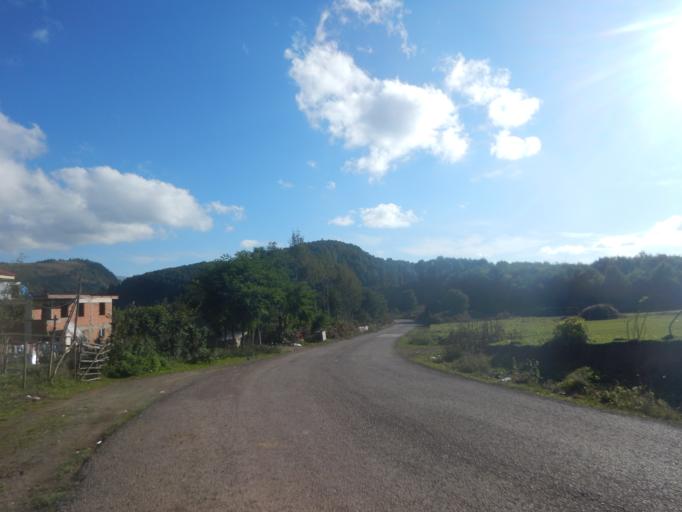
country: TR
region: Ordu
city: Golkoy
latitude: 40.6508
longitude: 37.5503
